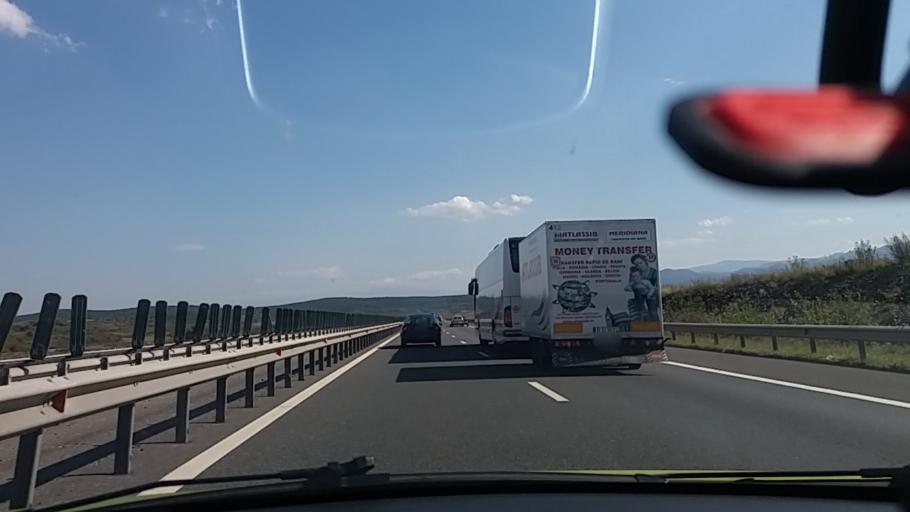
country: RO
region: Sibiu
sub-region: Oras Saliste
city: Saliste
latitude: 45.8020
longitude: 23.9212
